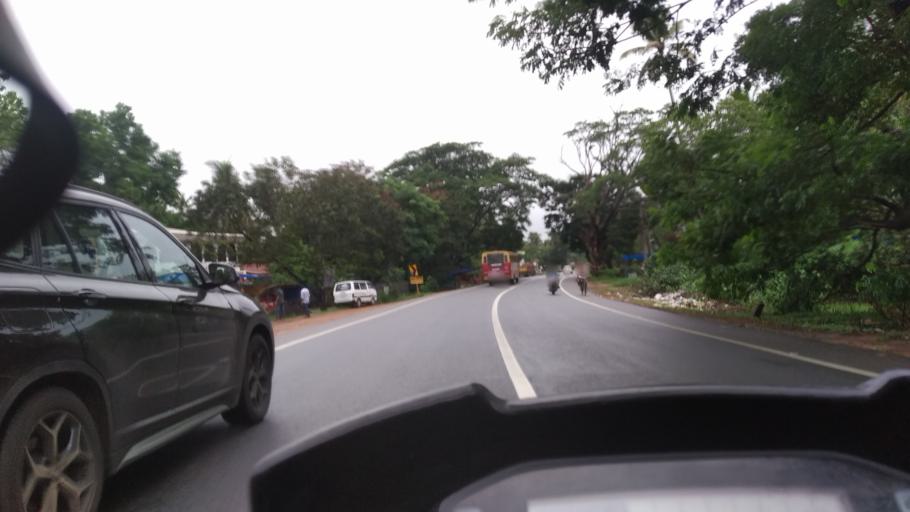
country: IN
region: Kerala
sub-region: Alappuzha
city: Mavelikara
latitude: 9.2847
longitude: 76.4400
